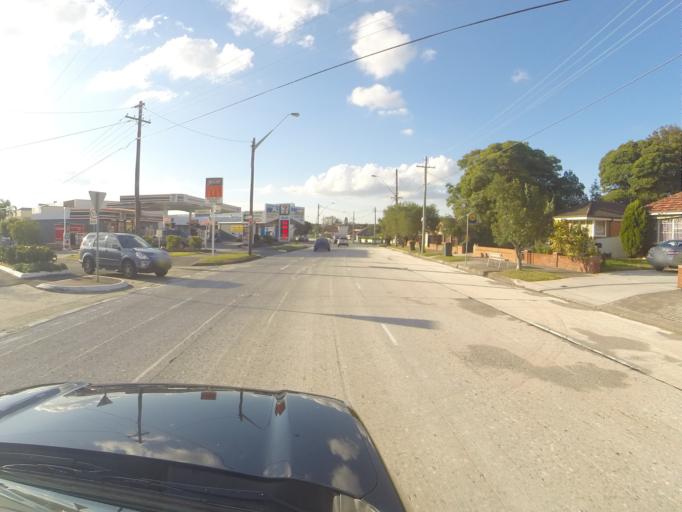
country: AU
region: New South Wales
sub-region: Rockdale
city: Bexley
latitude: -33.9560
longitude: 151.1185
